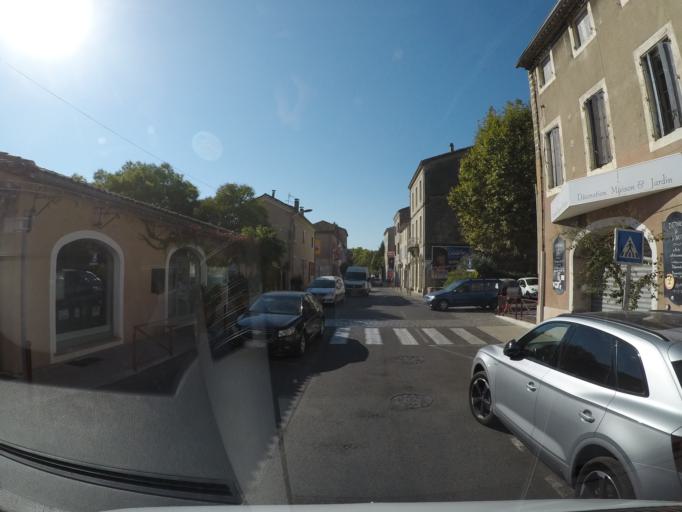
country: FR
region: Languedoc-Roussillon
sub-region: Departement du Gard
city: Anduze
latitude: 44.0527
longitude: 3.9853
